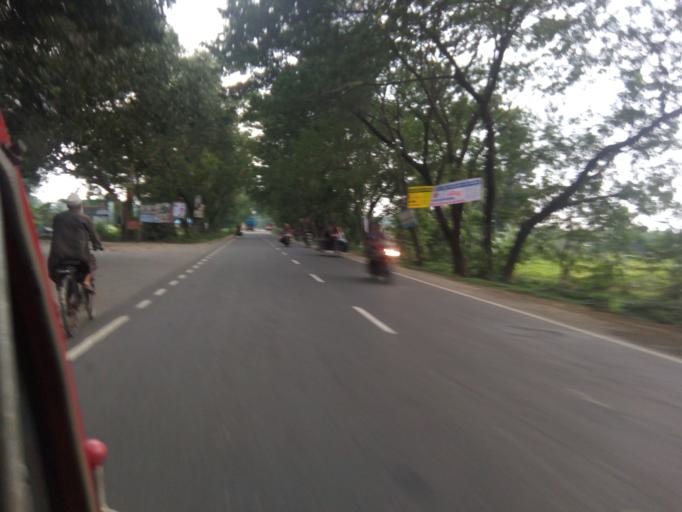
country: BD
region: Khulna
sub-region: Magura
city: Magura
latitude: 23.5322
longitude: 89.6150
